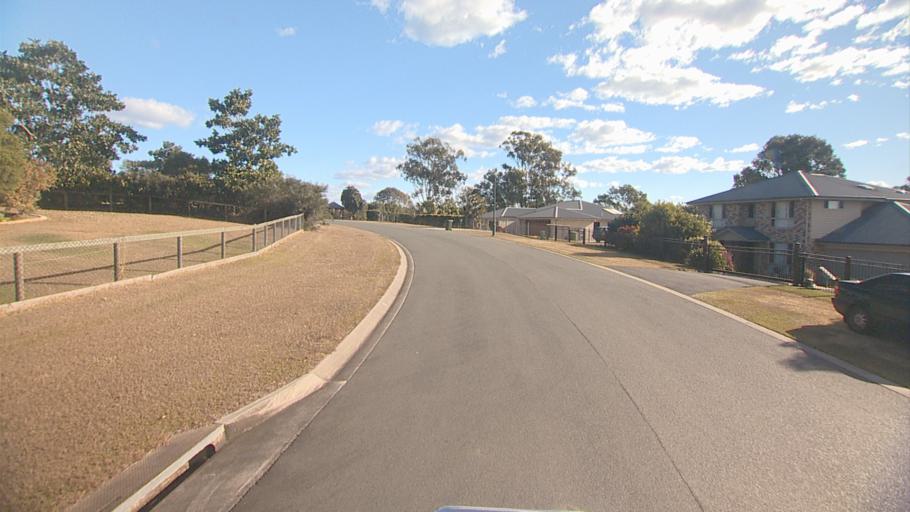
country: AU
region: Queensland
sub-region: Logan
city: North Maclean
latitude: -27.8264
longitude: 153.0018
